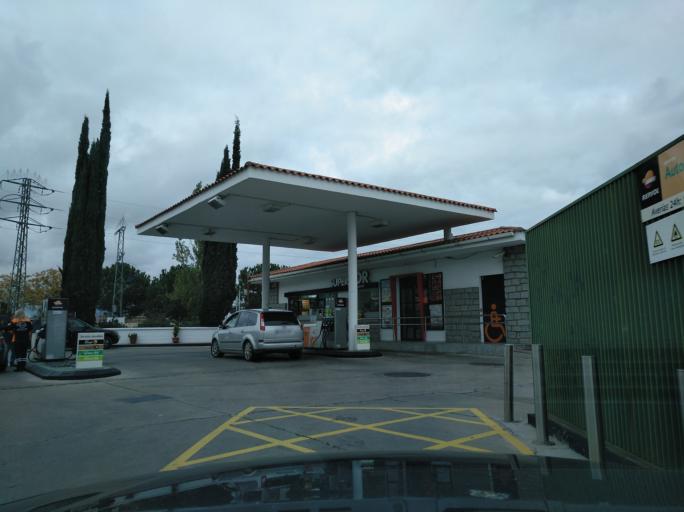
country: ES
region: Extremadura
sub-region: Provincia de Badajoz
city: Badajoz
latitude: 38.8817
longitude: -6.9640
